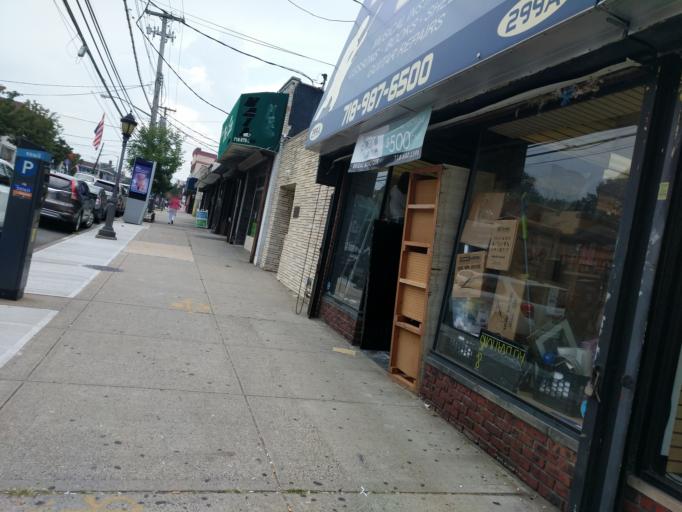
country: US
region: New York
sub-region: Richmond County
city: Staten Island
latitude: 40.5720
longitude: -74.1125
